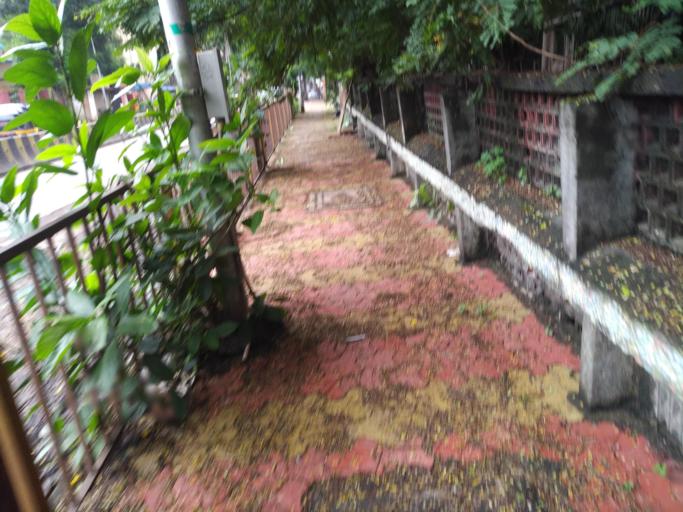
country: IN
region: Maharashtra
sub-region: Mumbai Suburban
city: Borivli
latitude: 19.2383
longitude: 72.8645
